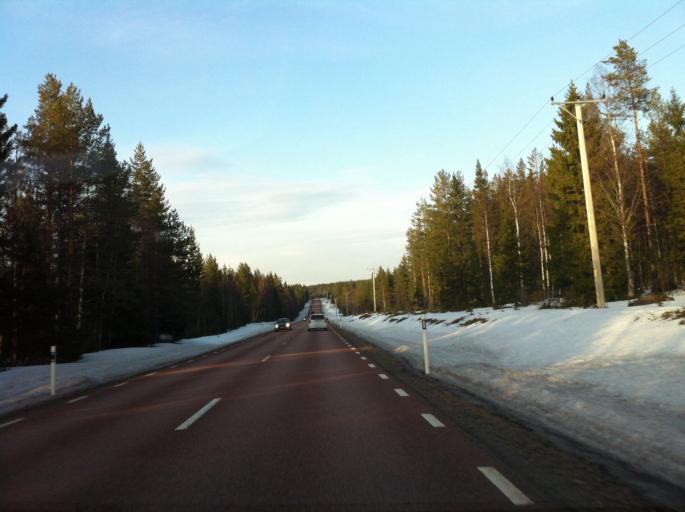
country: SE
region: Dalarna
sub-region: Vansbro Kommun
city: Vansbro
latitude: 60.3069
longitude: 14.1870
